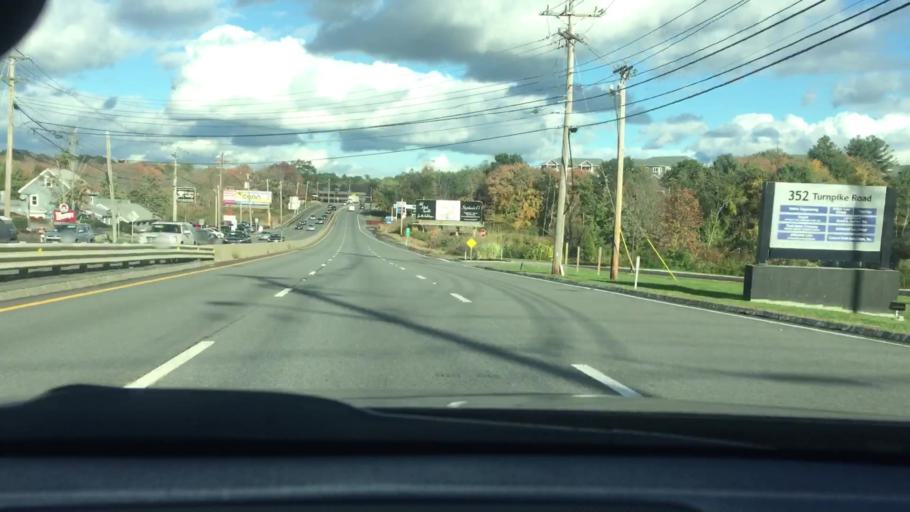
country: US
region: Massachusetts
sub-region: Worcester County
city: Southborough
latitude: 42.2892
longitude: -71.5586
